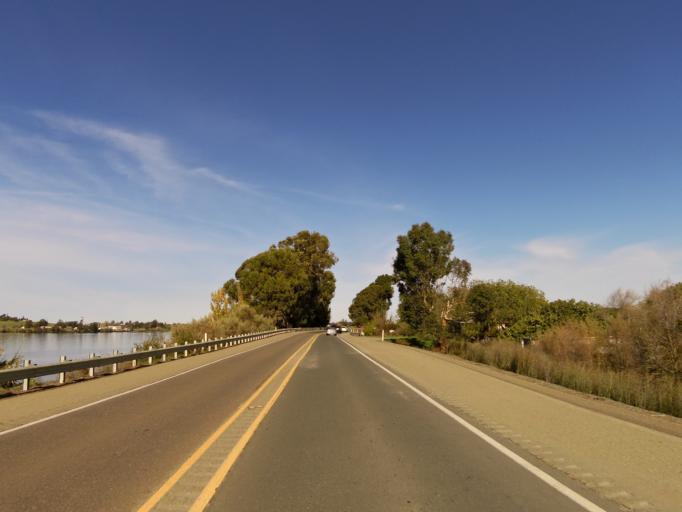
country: US
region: California
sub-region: Solano County
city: Rio Vista
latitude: 38.1363
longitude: -121.6862
